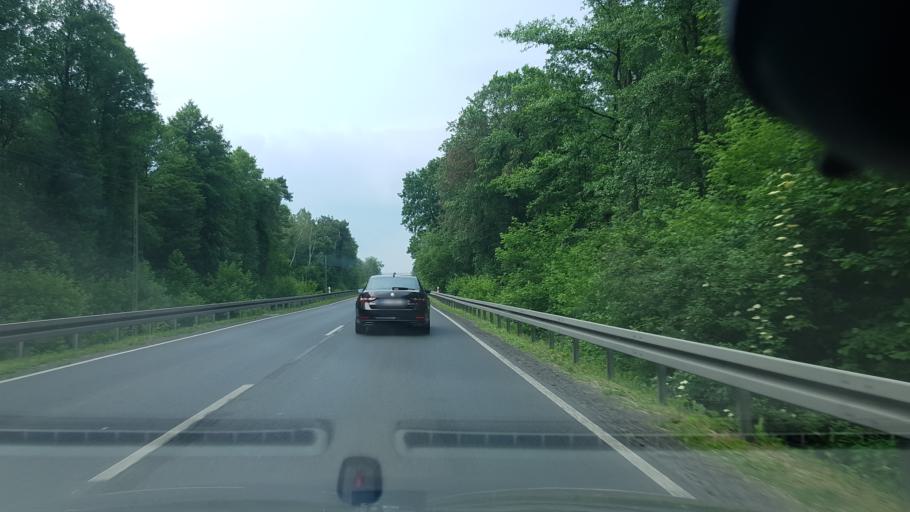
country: PL
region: Masovian Voivodeship
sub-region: Powiat legionowski
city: Wieliszew
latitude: 52.4400
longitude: 20.9952
